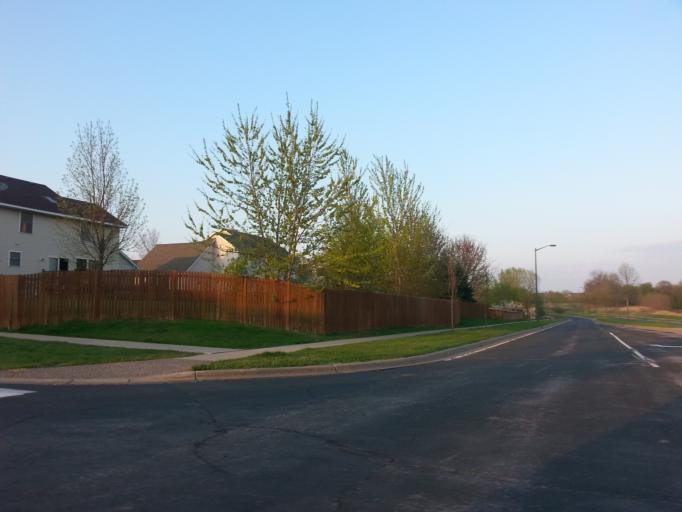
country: US
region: Minnesota
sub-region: Scott County
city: Prior Lake
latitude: 44.7395
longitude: -93.4287
